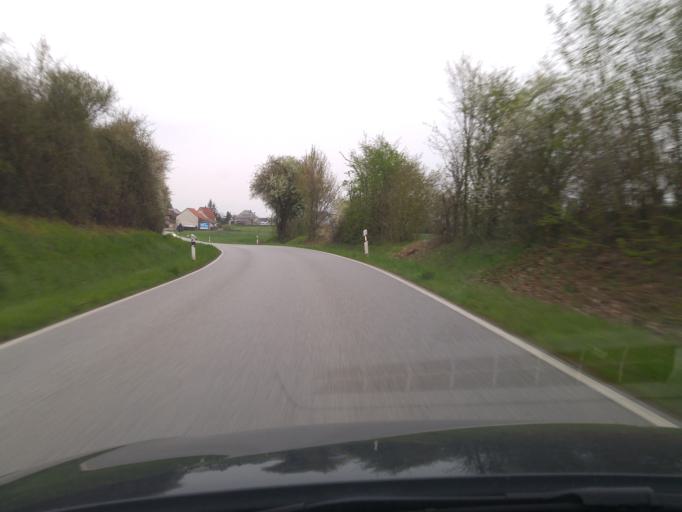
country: DE
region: Baden-Wuerttemberg
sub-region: Regierungsbezirk Stuttgart
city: Bad Rappenau
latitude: 49.2452
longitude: 9.1298
